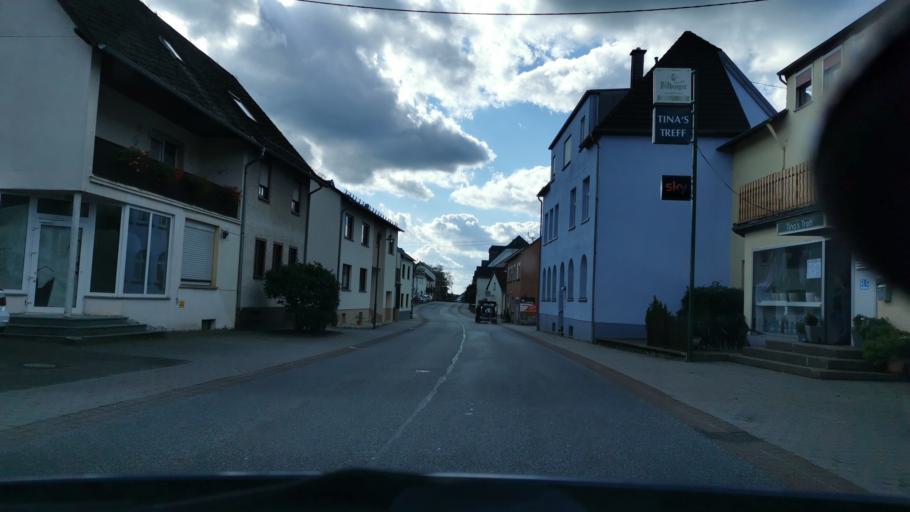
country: DE
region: Rheinland-Pfalz
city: Landscheid
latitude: 49.9867
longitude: 6.7709
